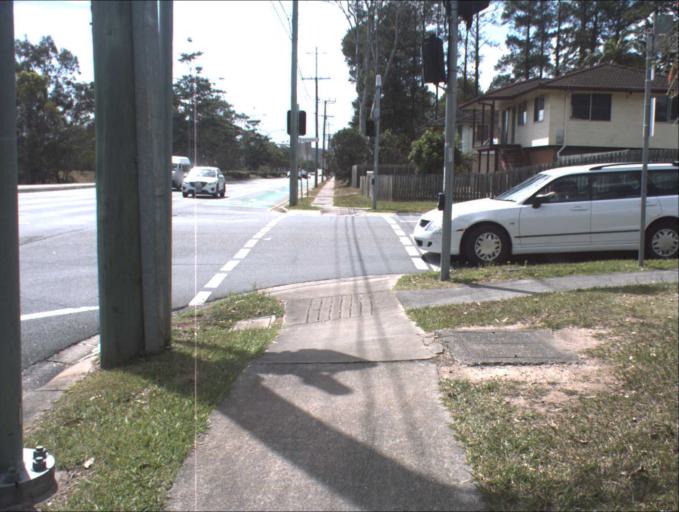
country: AU
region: Queensland
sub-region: Logan
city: Woodridge
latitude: -27.6183
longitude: 153.1010
